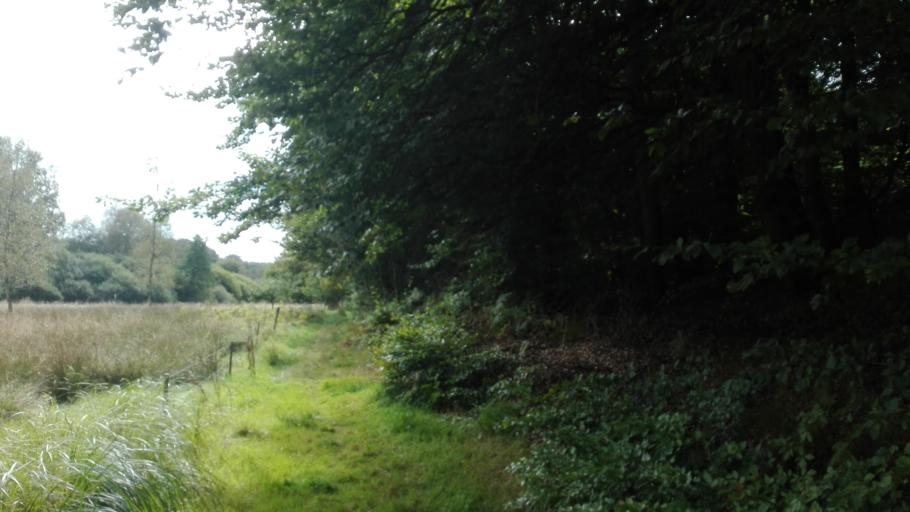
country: DK
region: Central Jutland
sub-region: Skanderborg Kommune
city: Stilling
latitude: 56.0970
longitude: 9.9822
